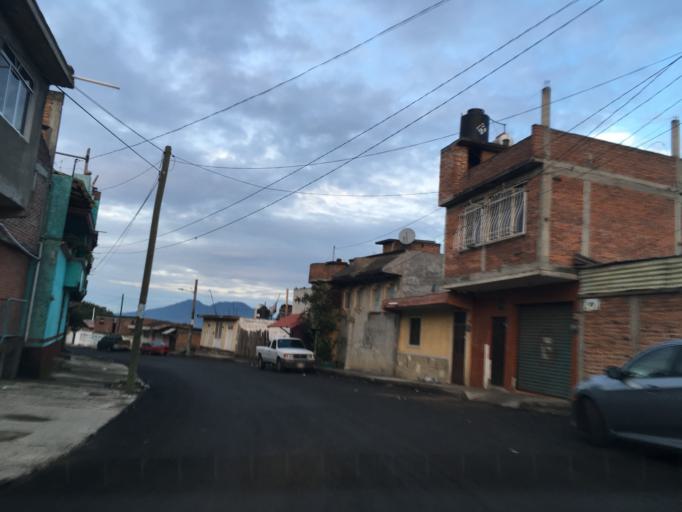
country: MX
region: Michoacan
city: Cheran
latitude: 19.6905
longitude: -101.9553
